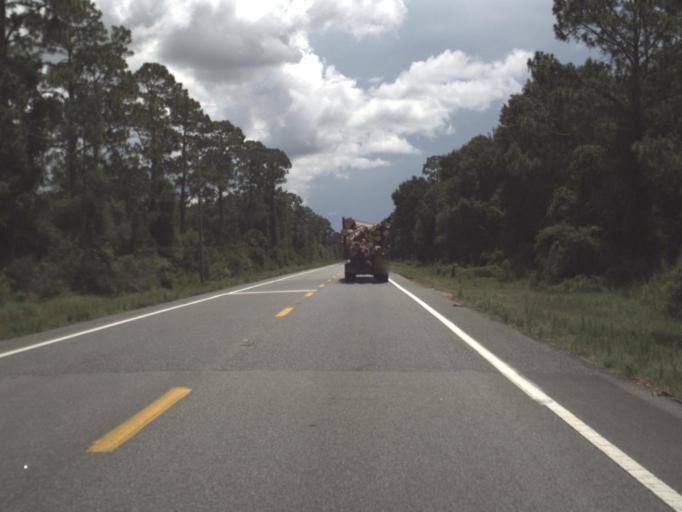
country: US
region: Florida
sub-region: Taylor County
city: Perry
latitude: 30.0992
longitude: -83.6939
